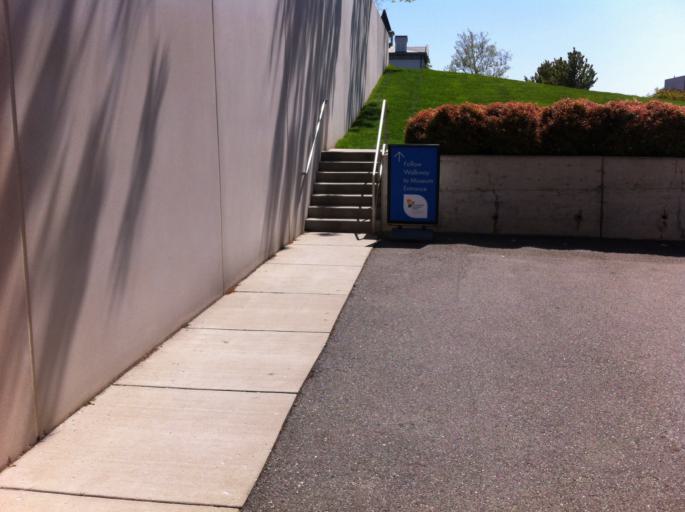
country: US
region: Virginia
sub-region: City of Richmond
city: Richmond
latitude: 37.5574
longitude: -77.4757
